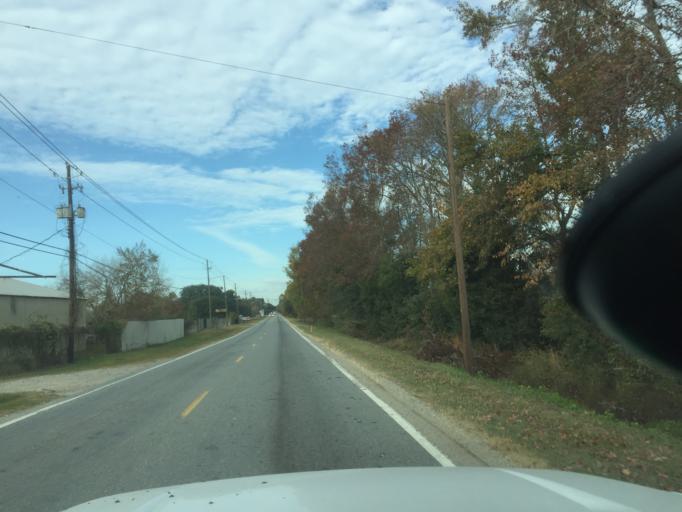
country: US
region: Georgia
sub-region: Chatham County
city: Savannah
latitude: 32.0820
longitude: -81.1227
